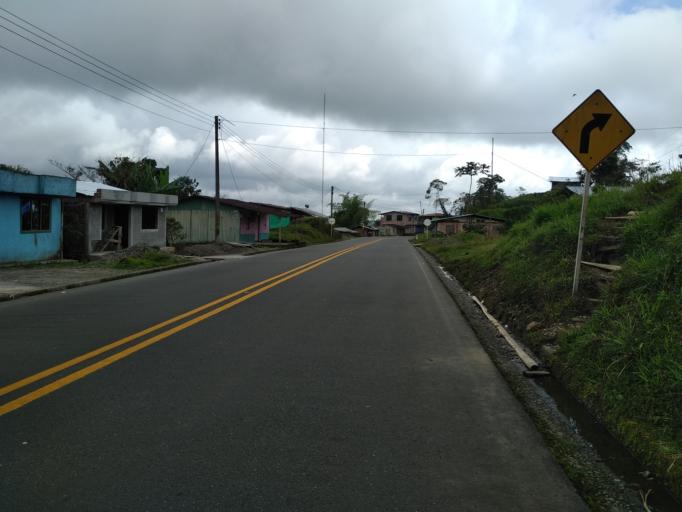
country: CO
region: Narino
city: Ricaurte
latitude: 1.3620
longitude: -78.1828
